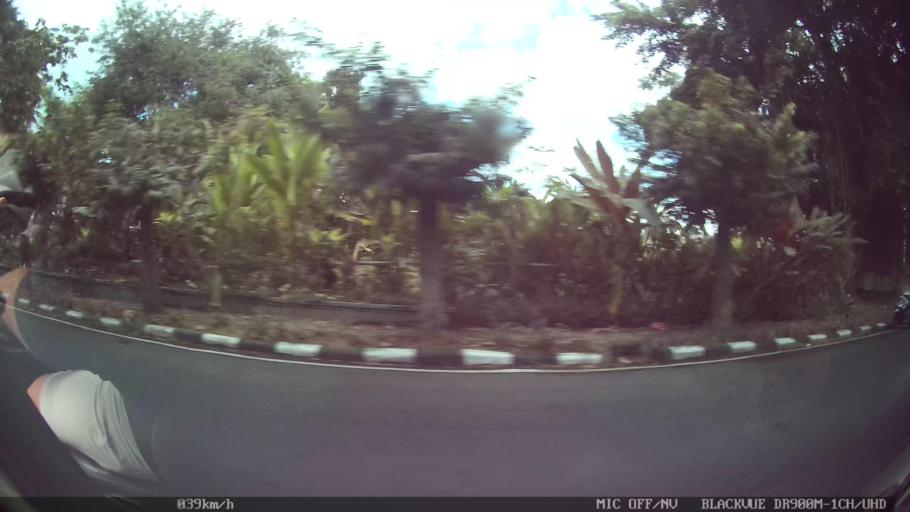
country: ID
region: Bali
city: Banjar Desa
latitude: -8.5814
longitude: 115.2806
